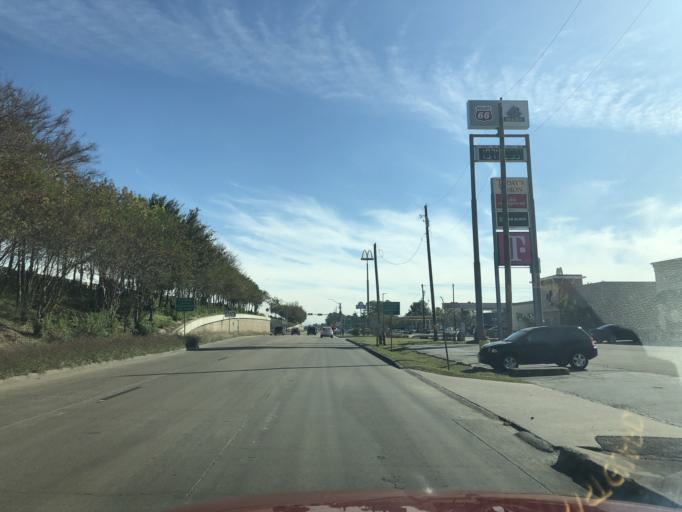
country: US
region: Texas
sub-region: Galveston County
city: Dickinson
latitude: 29.4503
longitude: -95.0784
